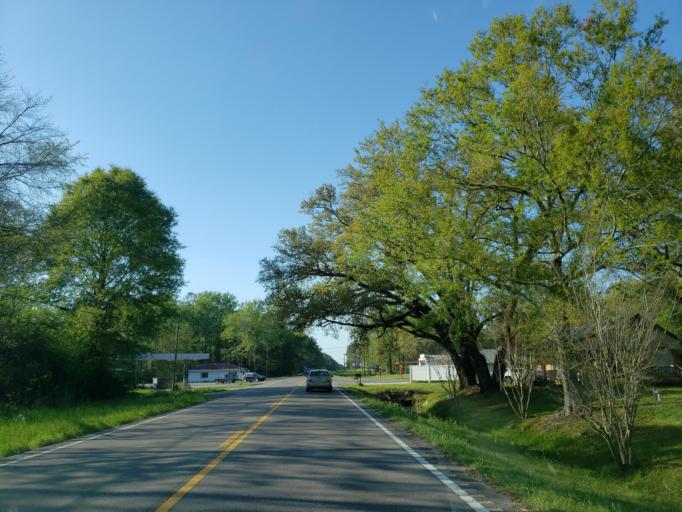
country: US
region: Mississippi
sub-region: Jones County
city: Laurel
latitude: 31.6264
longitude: -89.0897
